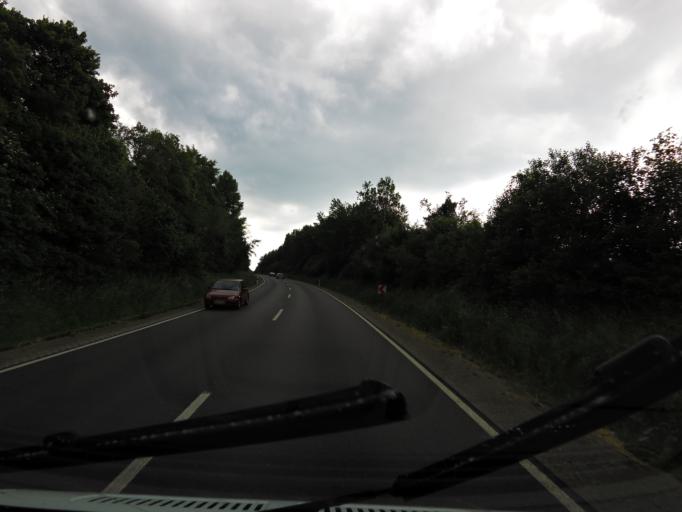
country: DE
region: Bavaria
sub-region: Lower Bavaria
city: Aicha vorm Wald
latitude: 48.6755
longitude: 13.2742
